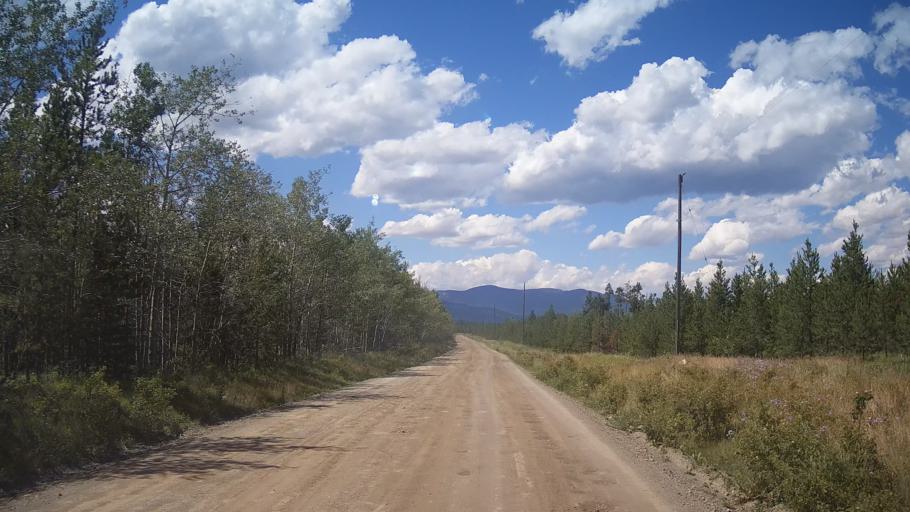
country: CA
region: British Columbia
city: Cache Creek
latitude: 51.2692
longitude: -121.7108
